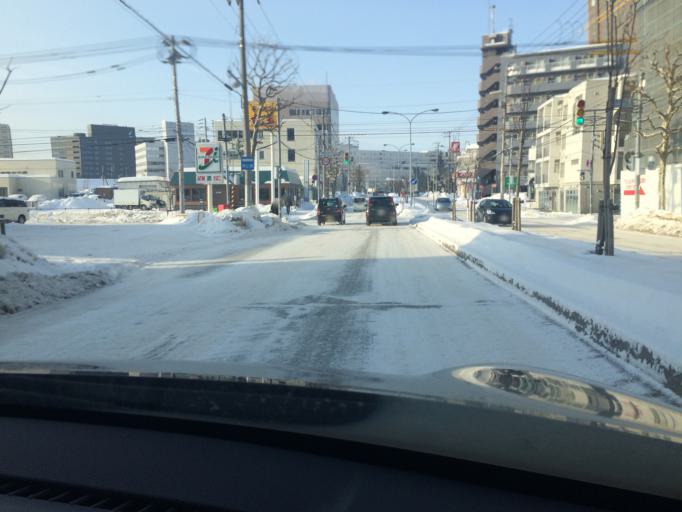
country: JP
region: Hokkaido
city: Ebetsu
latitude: 43.0411
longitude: 141.4771
